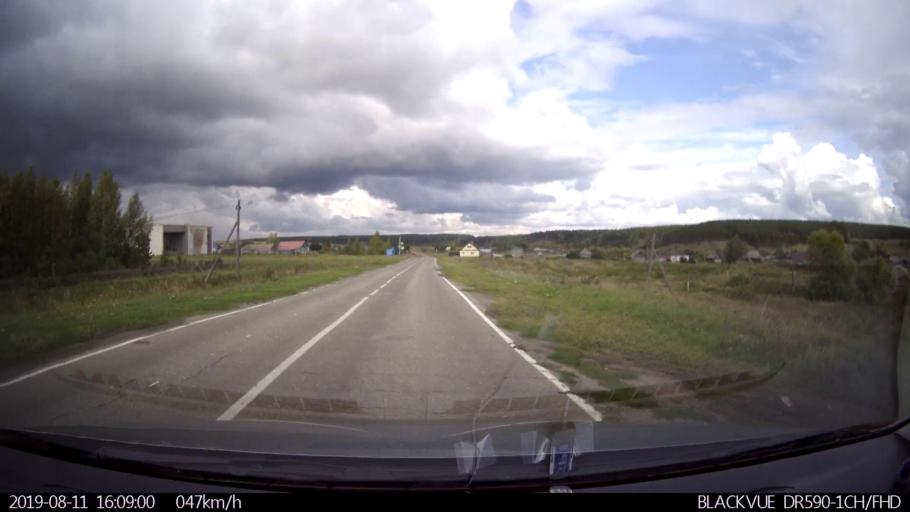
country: RU
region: Ulyanovsk
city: Ignatovka
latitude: 53.9892
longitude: 47.6508
